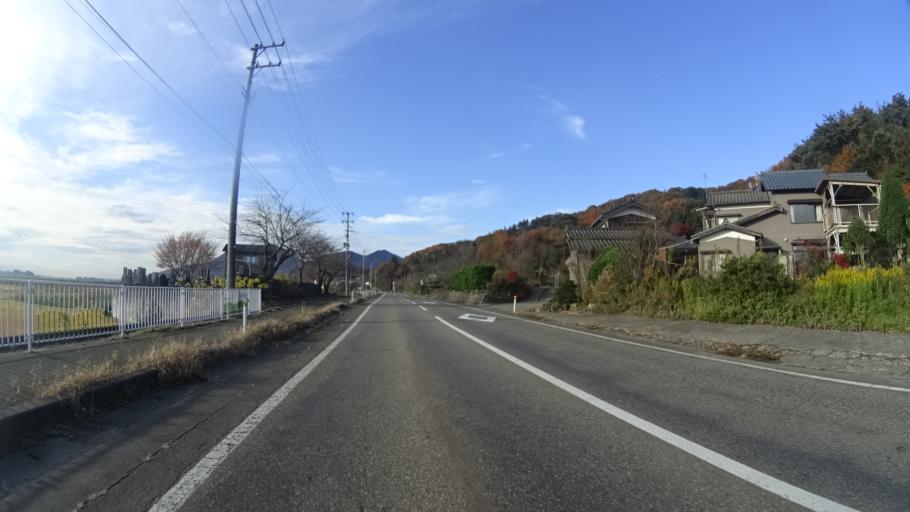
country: JP
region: Niigata
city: Yoshida-kasugacho
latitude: 37.6959
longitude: 138.8324
